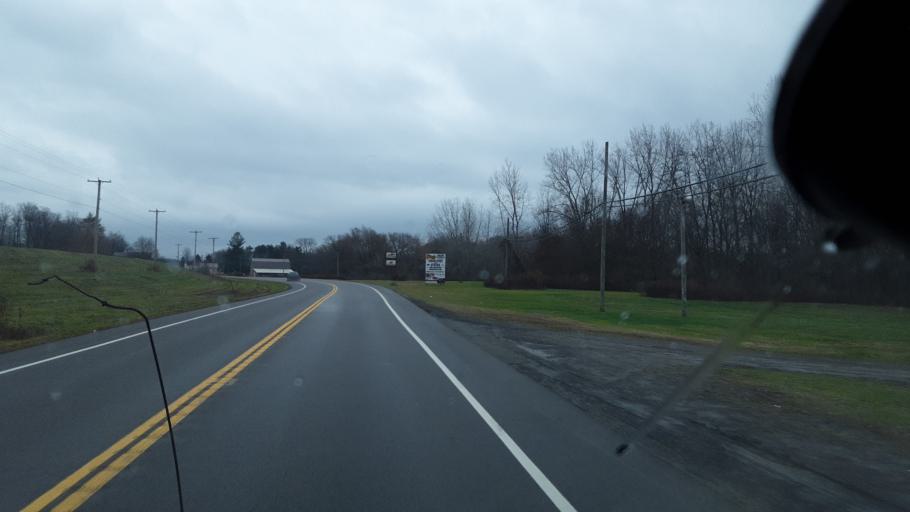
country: US
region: New York
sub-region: Wyoming County
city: Arcade
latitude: 42.4873
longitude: -78.3639
